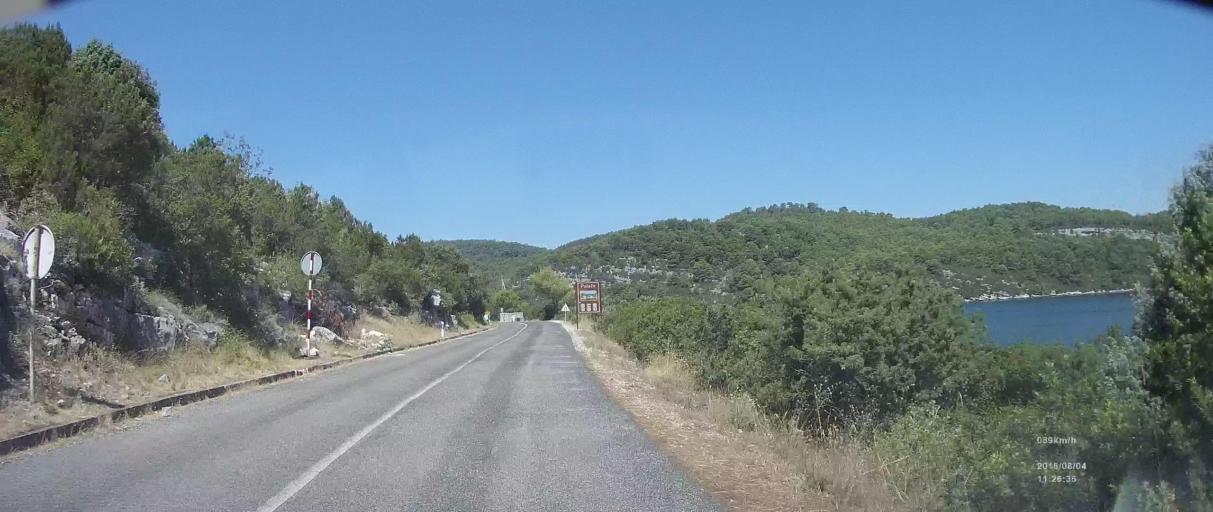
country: HR
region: Dubrovacko-Neretvanska
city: Blato
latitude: 42.7870
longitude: 17.3875
